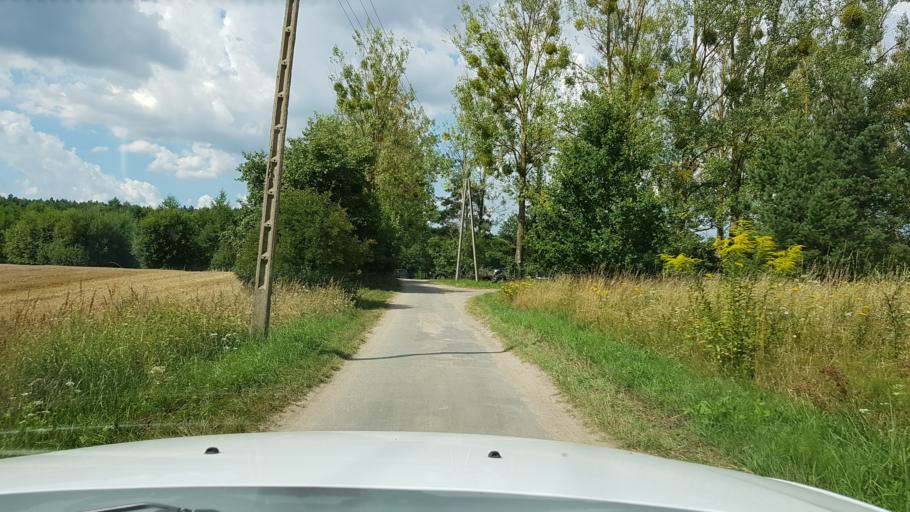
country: PL
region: West Pomeranian Voivodeship
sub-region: Powiat gryfinski
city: Chojna
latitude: 52.9081
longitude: 14.4955
